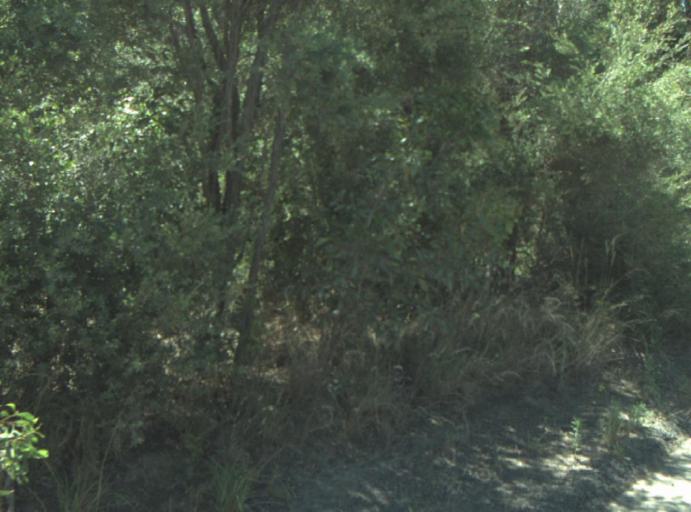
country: AU
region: Victoria
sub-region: Queenscliffe
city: Queenscliff
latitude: -38.1608
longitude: 144.7041
